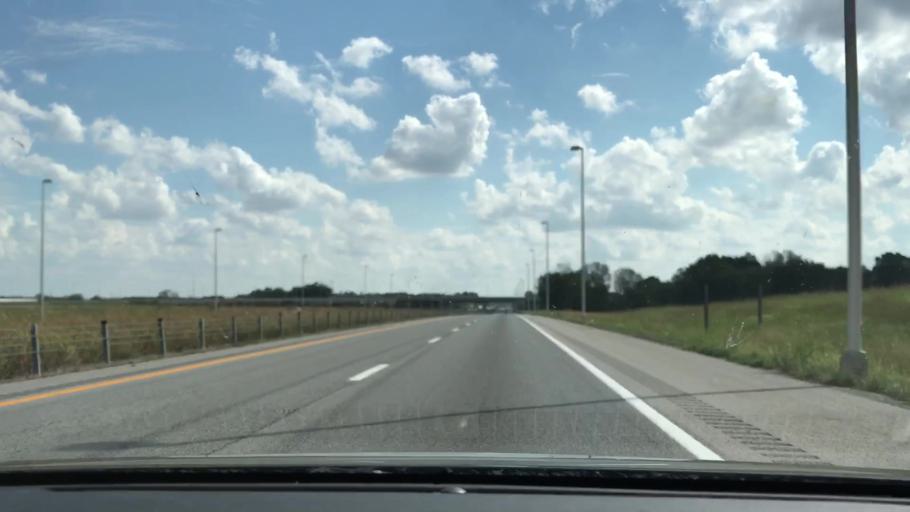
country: US
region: Kentucky
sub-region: Christian County
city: Fort Campbell North
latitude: 36.7469
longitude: -87.5163
